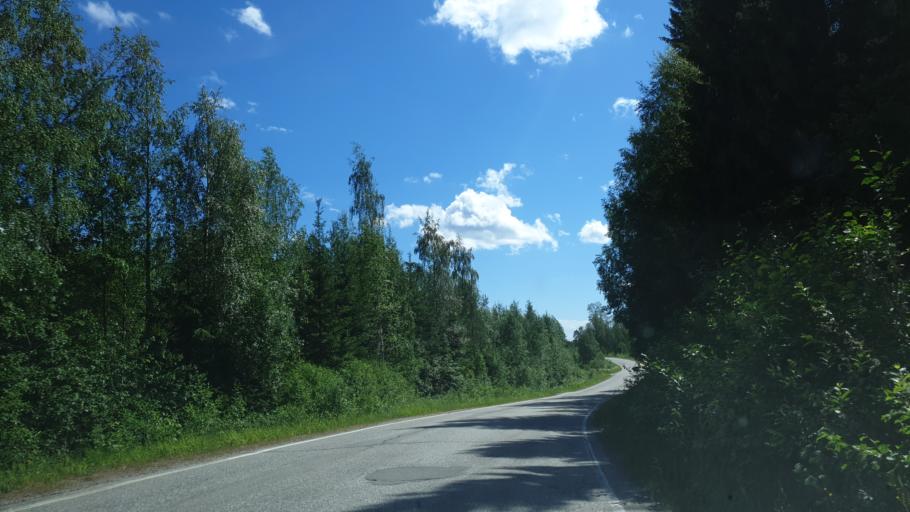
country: FI
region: Northern Savo
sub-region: Koillis-Savo
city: Kaavi
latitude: 62.9999
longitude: 28.5027
